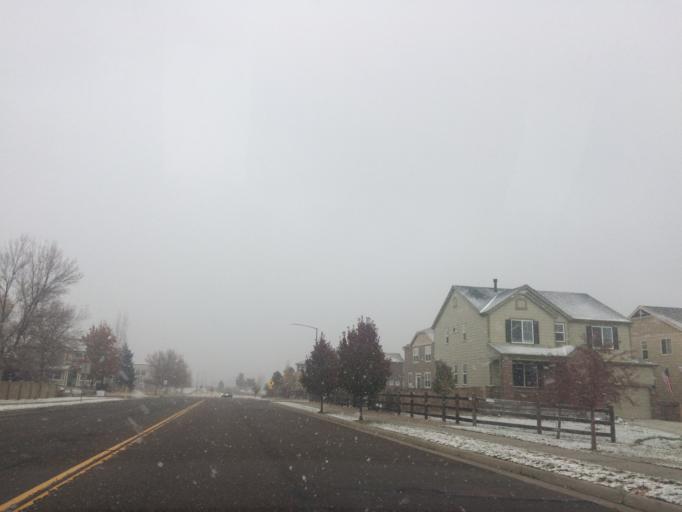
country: US
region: Colorado
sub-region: Boulder County
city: Erie
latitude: 40.0408
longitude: -105.0650
